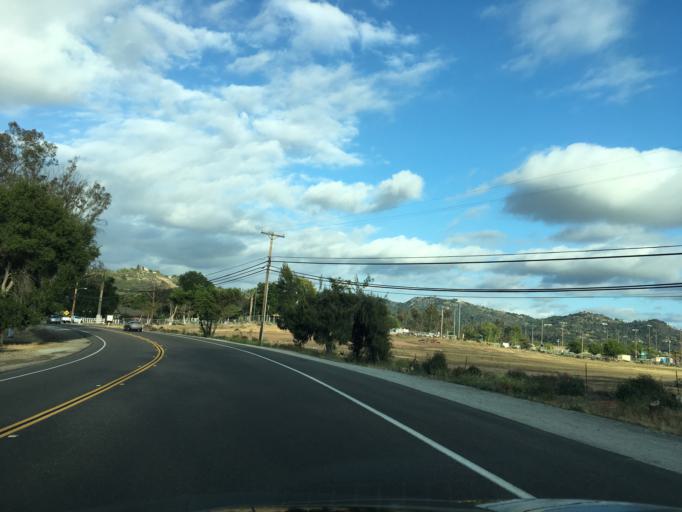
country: US
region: California
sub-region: San Diego County
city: Valley Center
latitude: 33.2226
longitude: -117.0412
